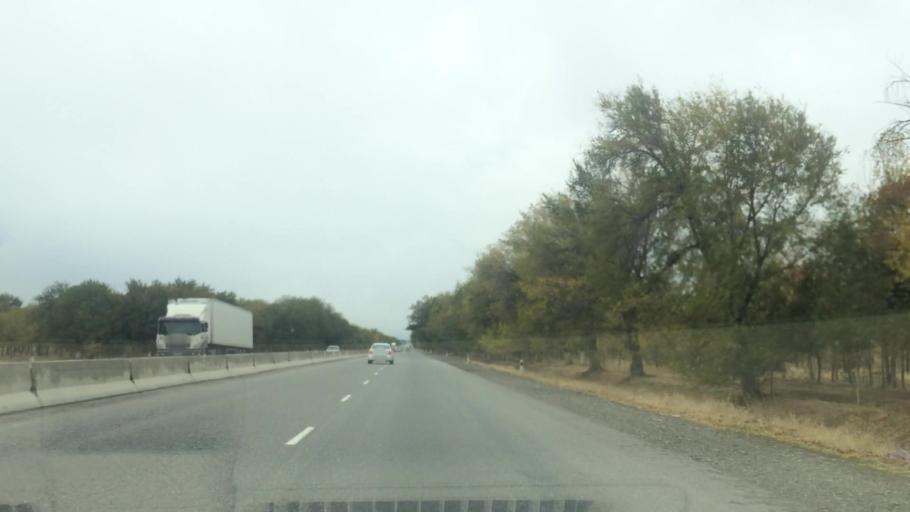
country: UZ
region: Samarqand
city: Bulung'ur
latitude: 39.8007
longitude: 67.3432
